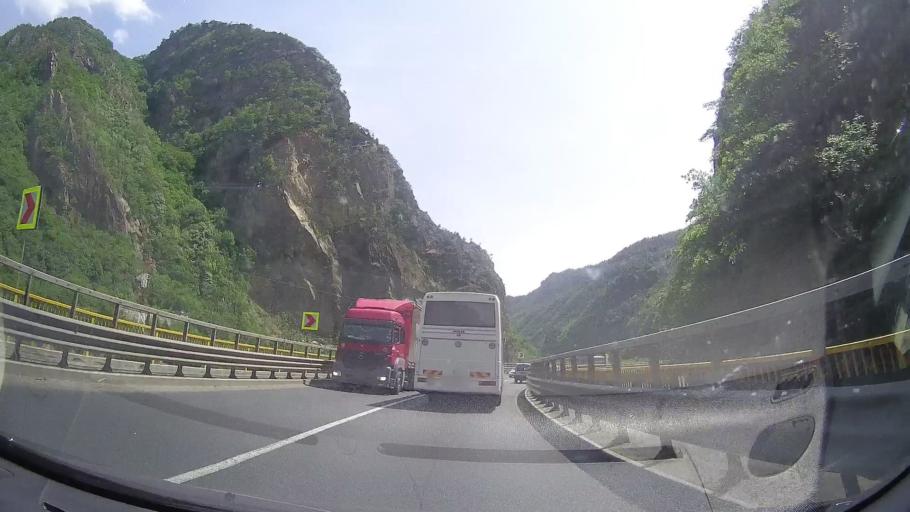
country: RO
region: Valcea
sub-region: Comuna Brezoi
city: Brezoi
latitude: 45.2979
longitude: 24.2897
